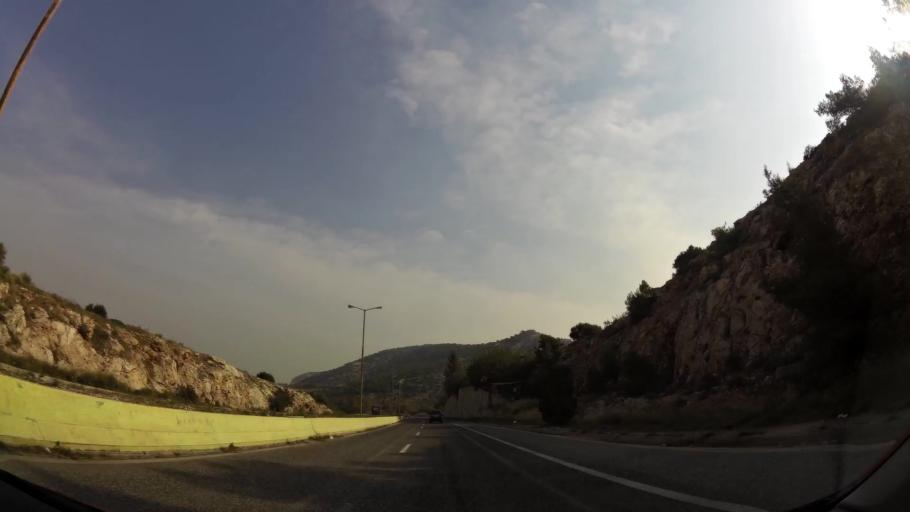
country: GR
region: Attica
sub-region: Nomarchia Athinas
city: Skaramangas
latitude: 38.0319
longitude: 23.6327
